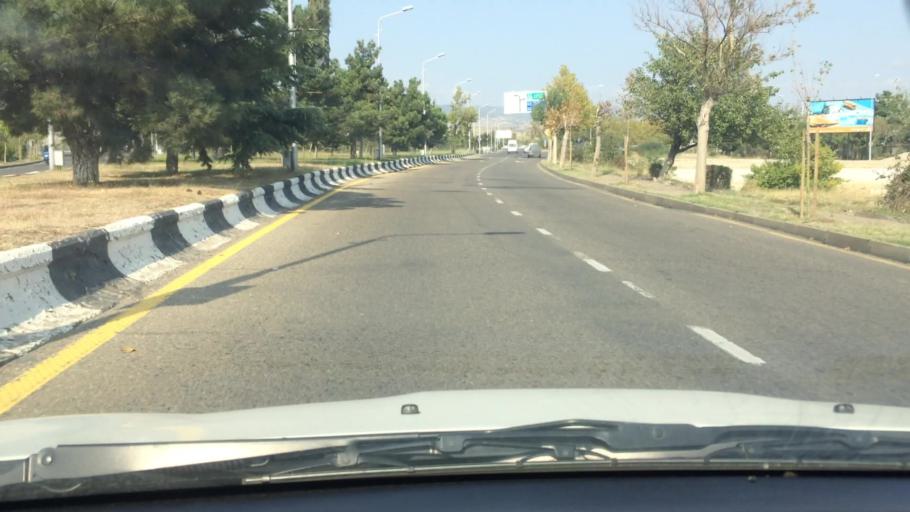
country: GE
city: Didi Lilo
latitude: 41.6899
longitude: 44.9530
